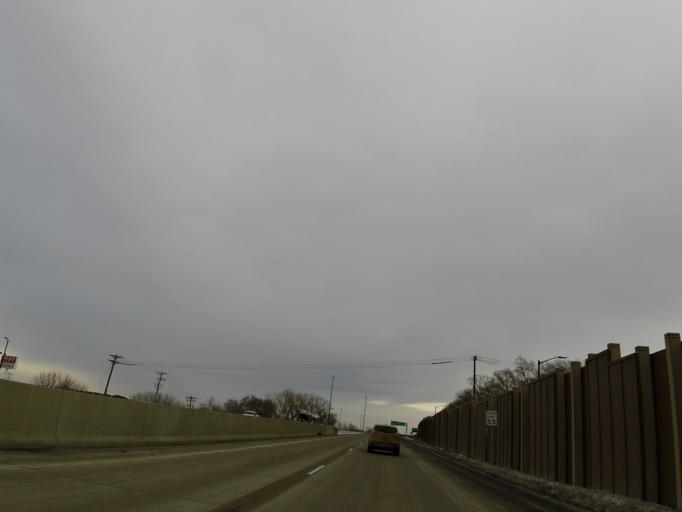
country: US
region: Minnesota
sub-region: Dakota County
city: Burnsville
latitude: 44.7736
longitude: -93.2971
